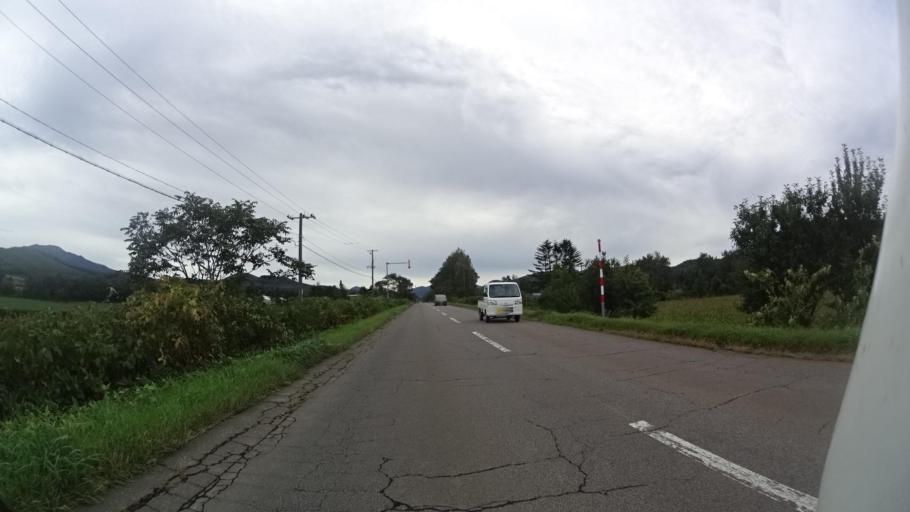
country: JP
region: Hokkaido
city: Shibetsu
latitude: 43.8652
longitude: 144.7543
